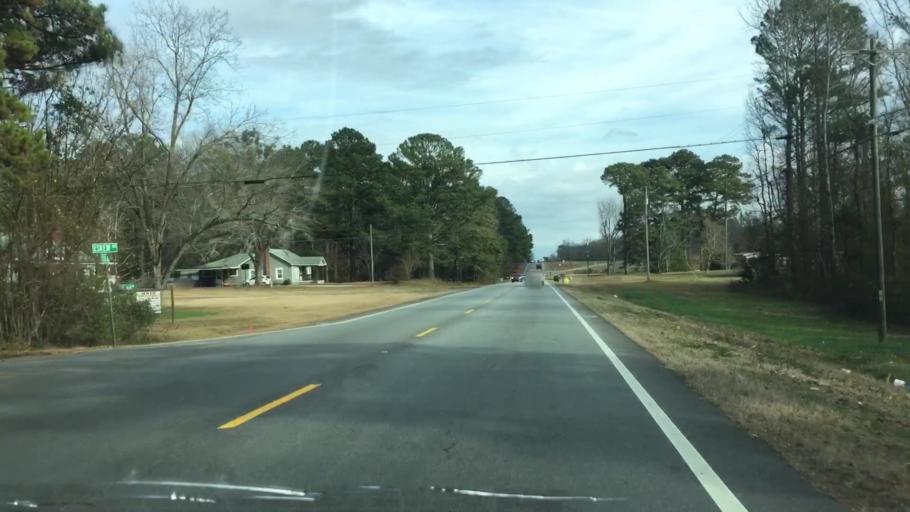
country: US
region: Georgia
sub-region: Henry County
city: McDonough
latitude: 33.4322
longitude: -84.0543
